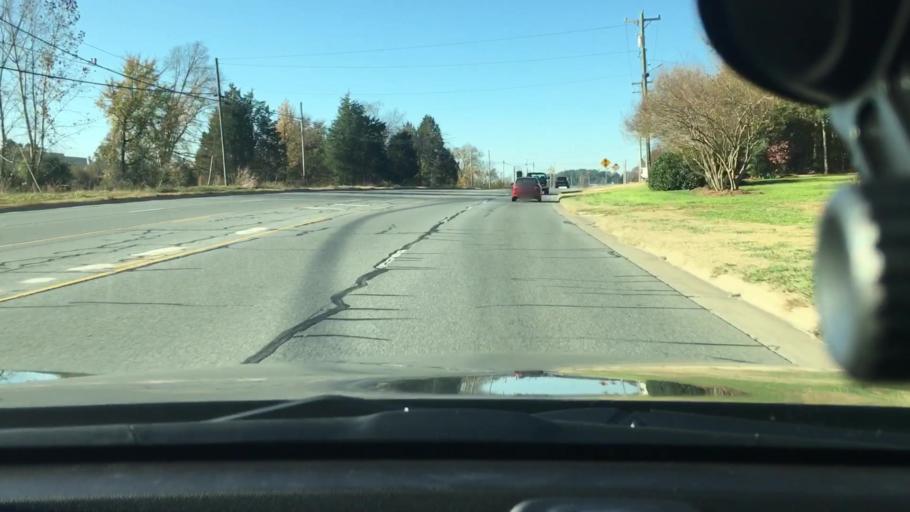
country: US
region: North Carolina
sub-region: Cabarrus County
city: Harrisburg
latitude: 35.3261
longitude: -80.6369
